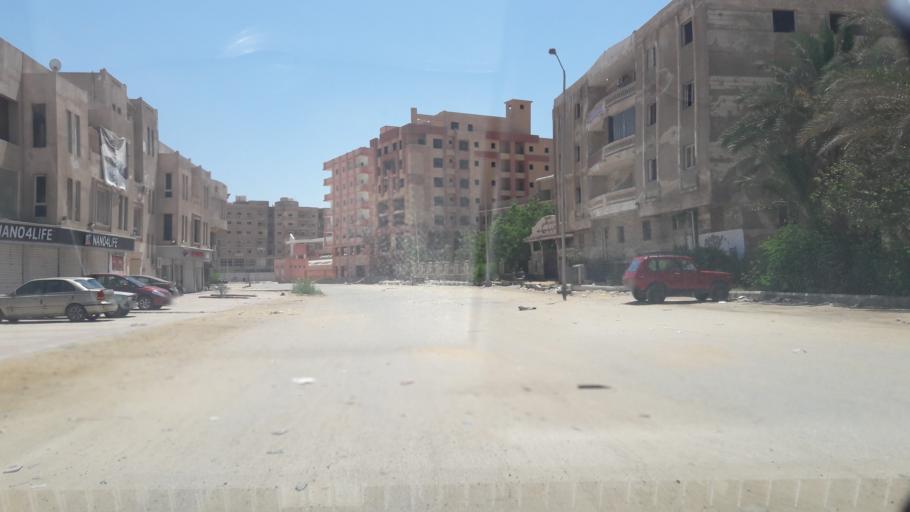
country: EG
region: Al Jizah
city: Madinat Sittah Uktubar
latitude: 29.9676
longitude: 30.9334
